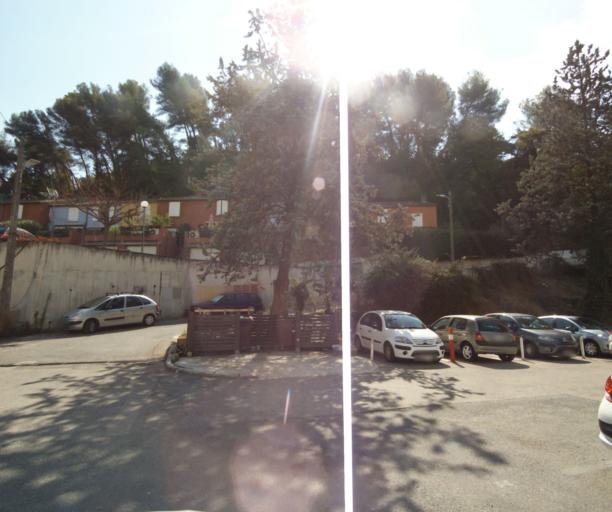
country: FR
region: Provence-Alpes-Cote d'Azur
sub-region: Departement des Alpes-Maritimes
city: Drap
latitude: 43.7515
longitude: 7.3217
